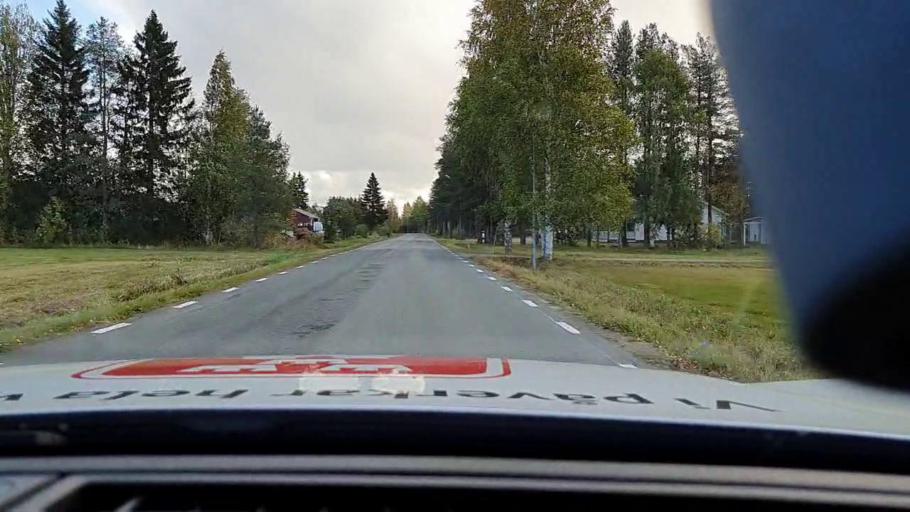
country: SE
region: Vaesterbotten
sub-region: Skelleftea Kommun
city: Langsele
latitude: 64.9489
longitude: 19.9312
